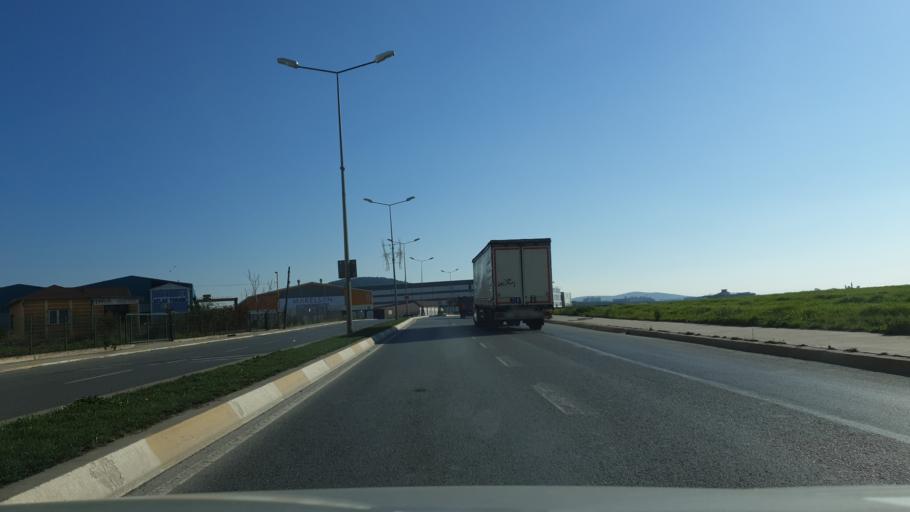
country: TR
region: Istanbul
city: Icmeler
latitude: 40.8881
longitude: 29.3528
